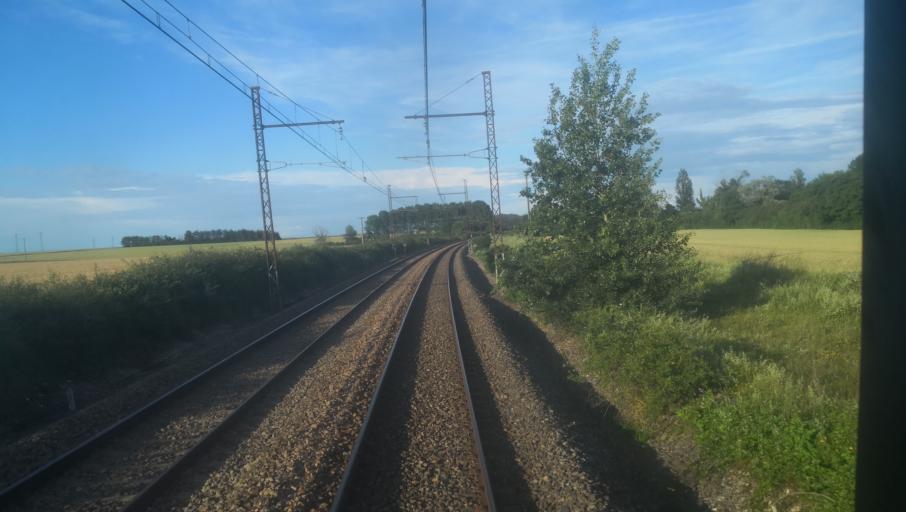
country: FR
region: Centre
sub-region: Departement de l'Indre
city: Neuvy-Pailloux
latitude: 46.9147
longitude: 1.9271
